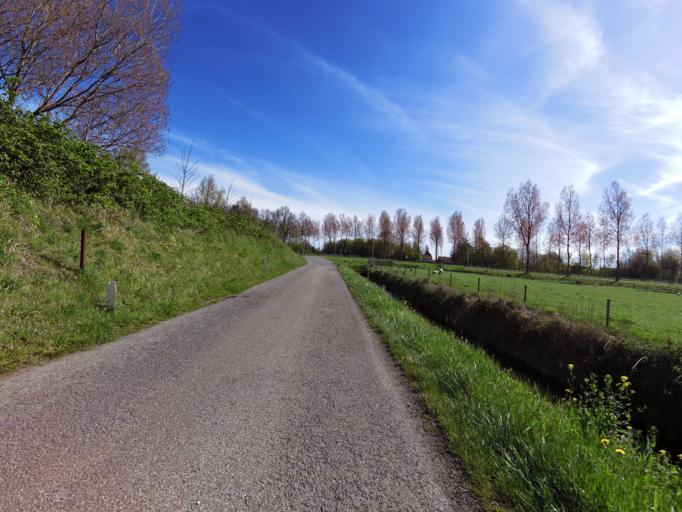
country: NL
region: South Holland
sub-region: Gemeente Brielle
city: Brielle
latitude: 51.9165
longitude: 4.1134
